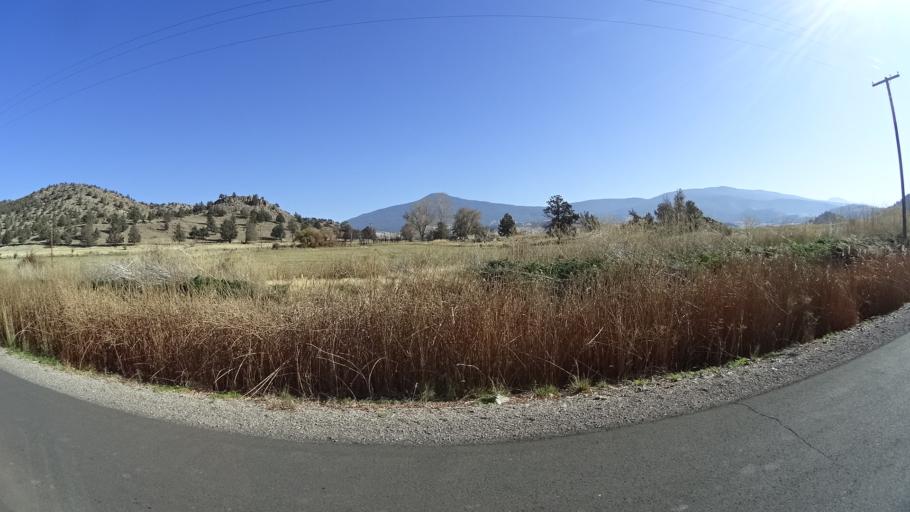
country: US
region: California
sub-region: Siskiyou County
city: Montague
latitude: 41.7008
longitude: -122.3762
